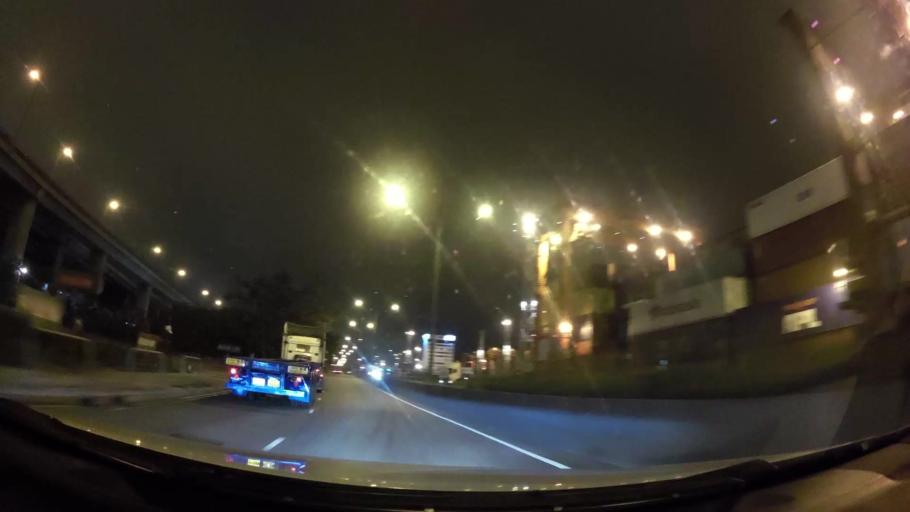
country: HK
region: Sham Shui Po
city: Sham Shui Po
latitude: 22.3385
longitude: 114.1311
